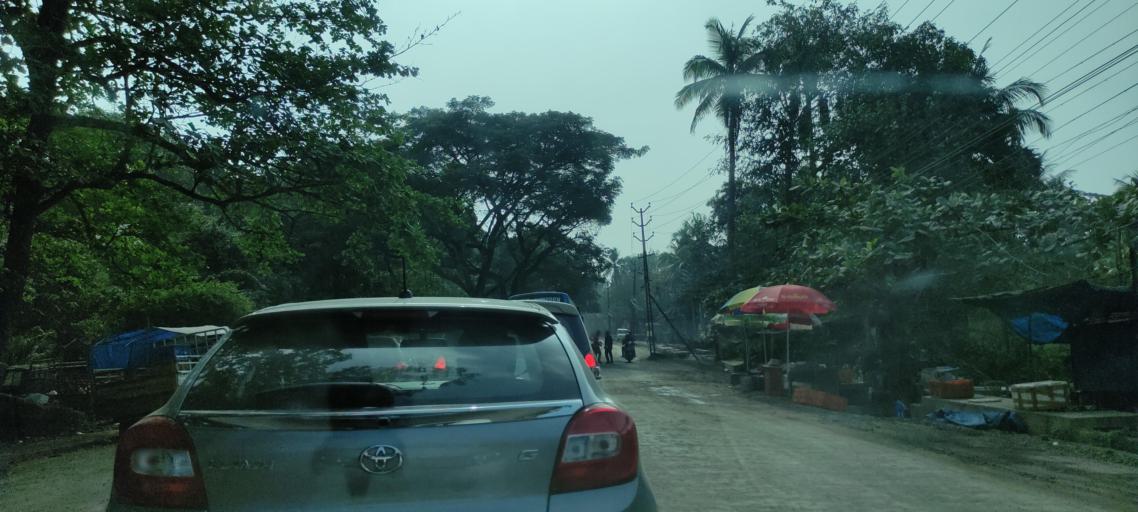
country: IN
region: Kerala
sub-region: Pattanamtitta
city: Tiruvalla
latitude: 9.3692
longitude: 76.5483
